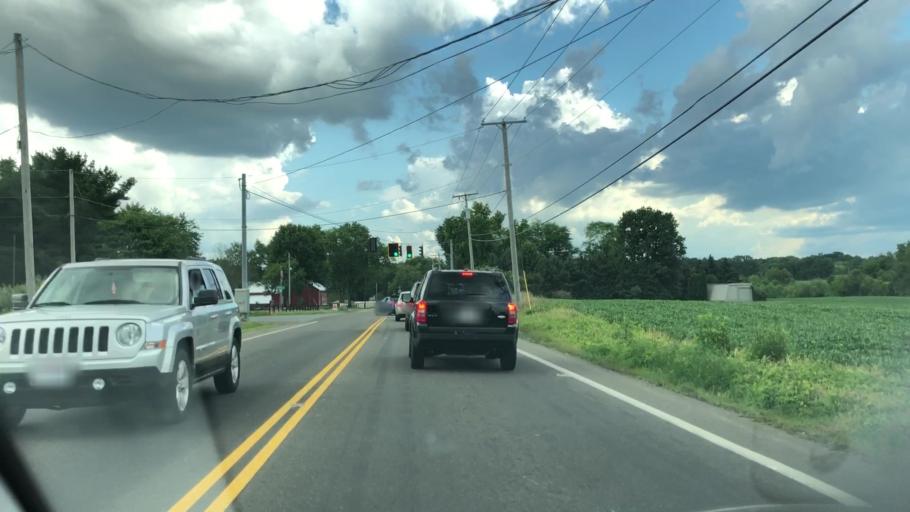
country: US
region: Ohio
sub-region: Summit County
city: Greensburg
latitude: 40.9012
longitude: -81.4670
